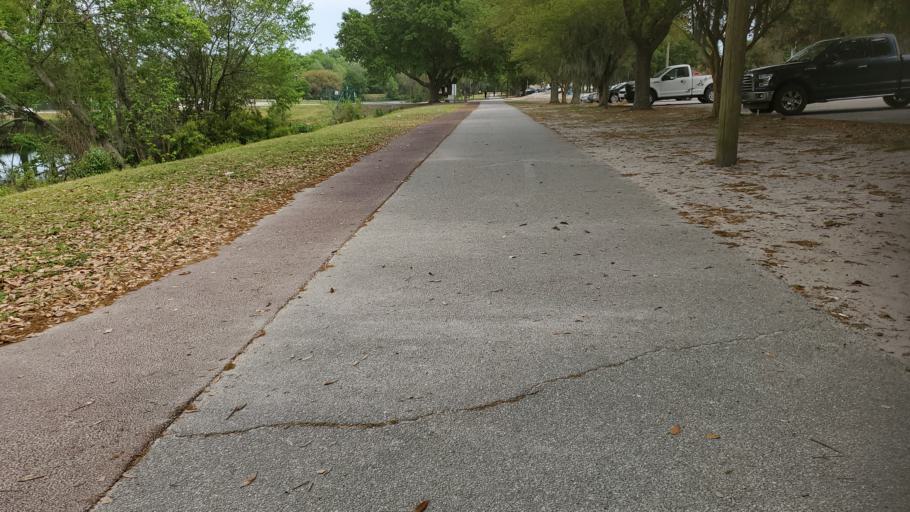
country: US
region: Georgia
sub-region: Chatham County
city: Isle of Hope
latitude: 31.9908
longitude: -81.0888
